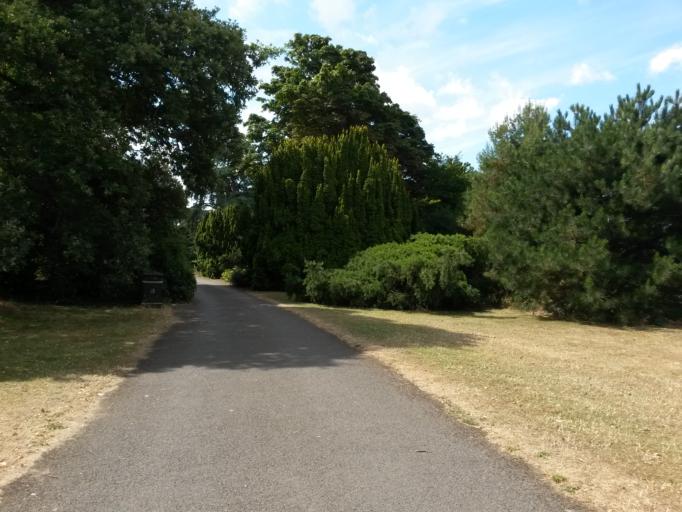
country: GB
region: England
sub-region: Greater London
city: Brentford
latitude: 51.4763
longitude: -0.3048
